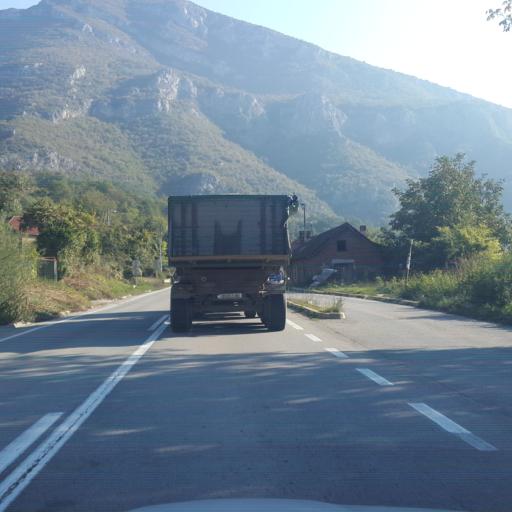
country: RS
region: Central Serbia
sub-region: Nisavski Okrug
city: Svrljig
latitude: 43.3342
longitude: 22.1199
